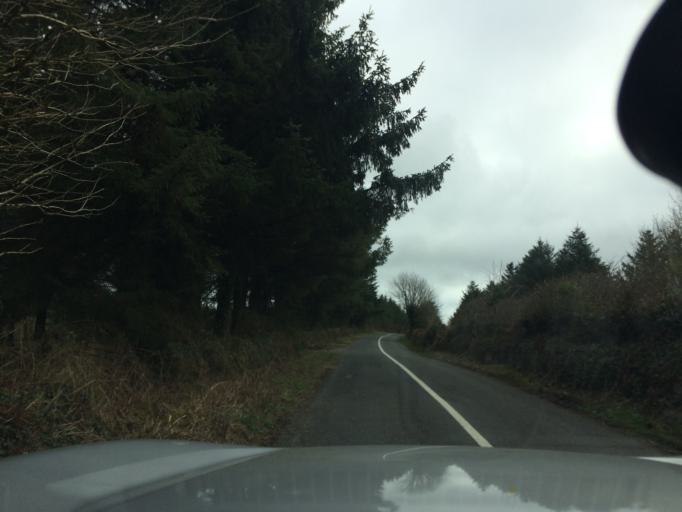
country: IE
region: Munster
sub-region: South Tipperary
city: Cluain Meala
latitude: 52.3367
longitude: -7.6222
